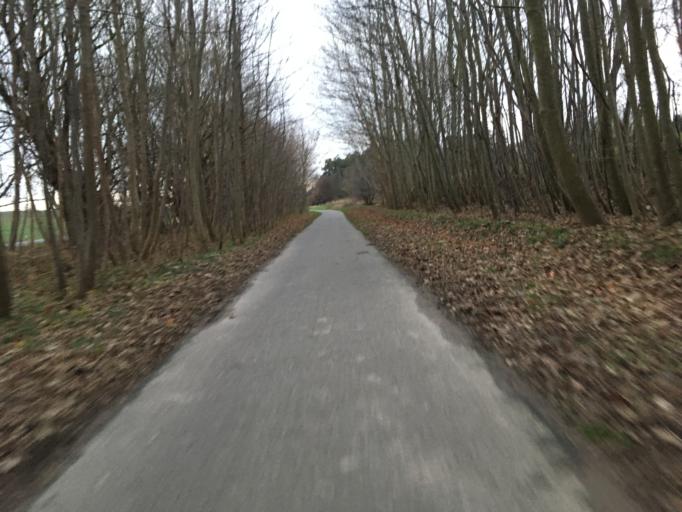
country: DE
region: Mecklenburg-Vorpommern
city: Sagard
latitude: 54.5074
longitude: 13.5948
